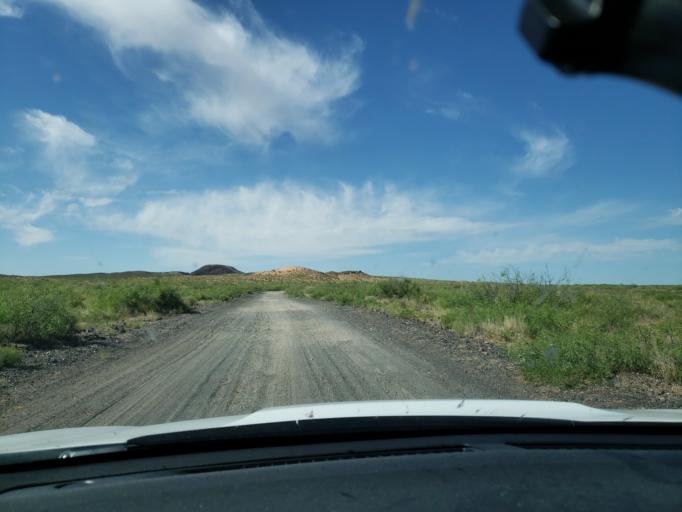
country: US
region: New Mexico
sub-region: Dona Ana County
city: San Miguel
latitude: 32.0859
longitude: -106.7881
